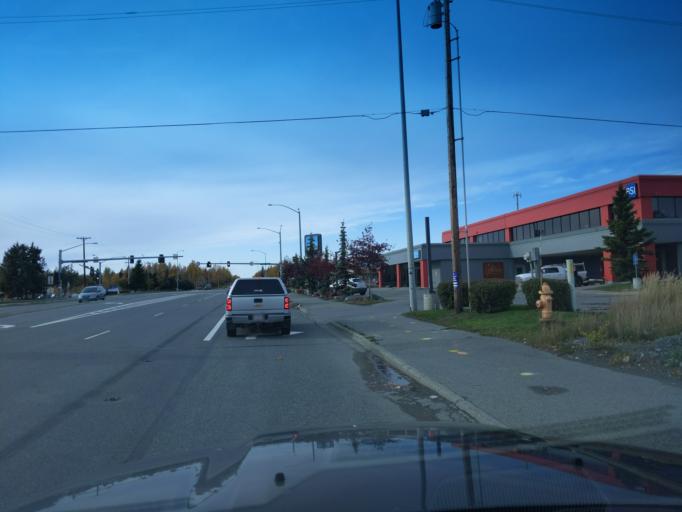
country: US
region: Alaska
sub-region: Anchorage Municipality
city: Anchorage
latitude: 61.1376
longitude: -149.9498
